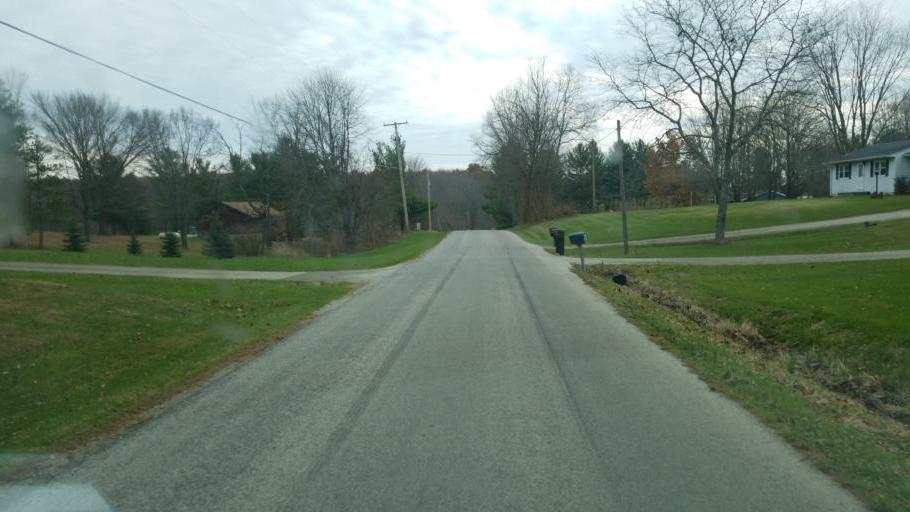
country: US
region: Ohio
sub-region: Richland County
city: Ontario
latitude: 40.7474
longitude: -82.6654
